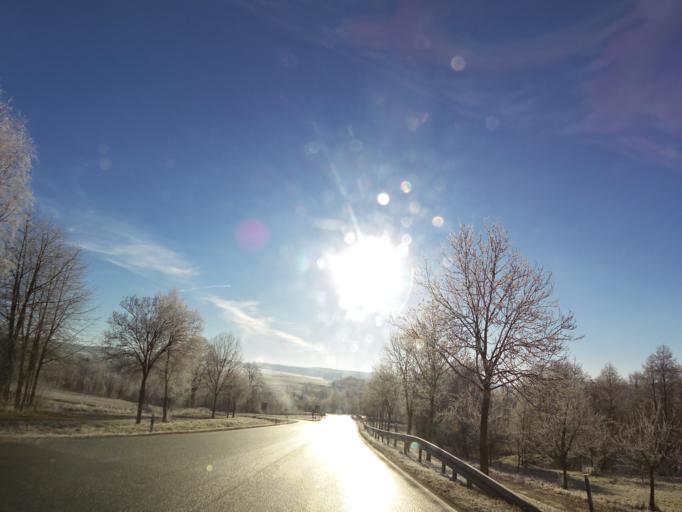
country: DE
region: Bavaria
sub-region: Upper Franconia
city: Bad Alexandersbad
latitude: 50.0249
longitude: 12.0170
